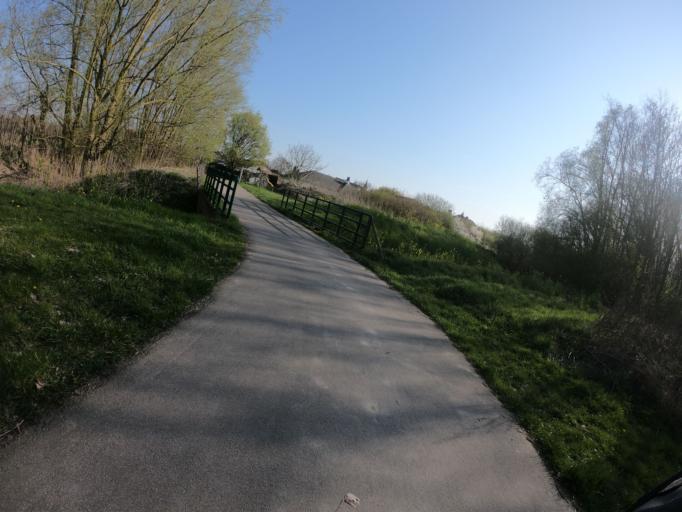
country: BE
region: Flanders
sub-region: Provincie Limburg
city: Sint-Truiden
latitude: 50.8166
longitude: 5.2335
